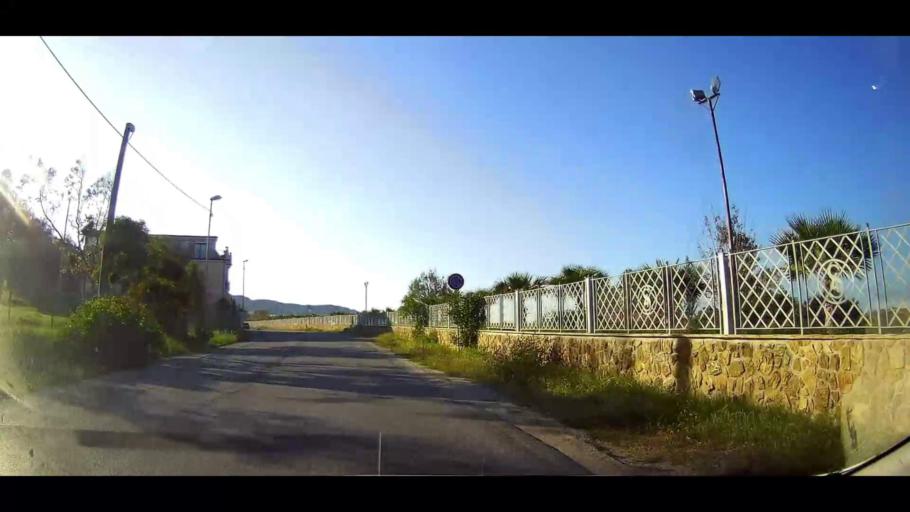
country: IT
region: Calabria
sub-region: Provincia di Crotone
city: Crotone
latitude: 39.0491
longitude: 17.1439
